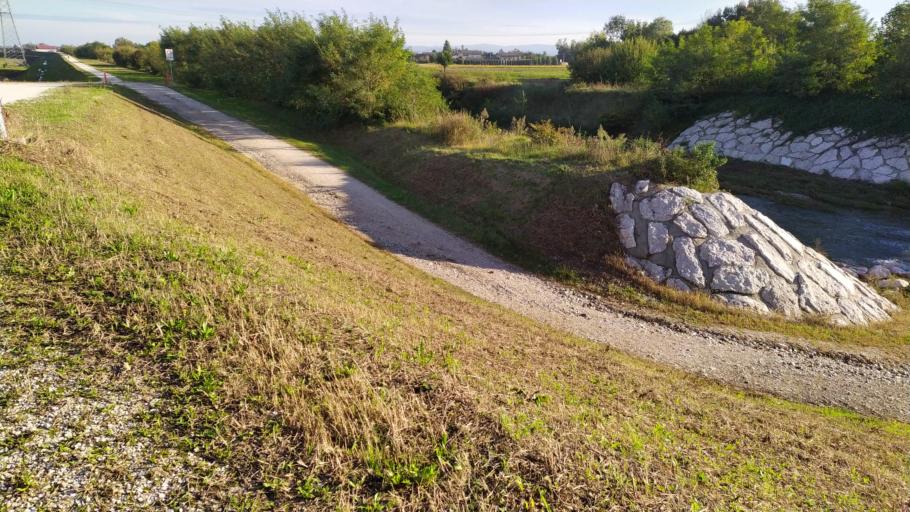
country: IT
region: Veneto
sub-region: Provincia di Vicenza
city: Novoledo
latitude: 45.6327
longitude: 11.4997
